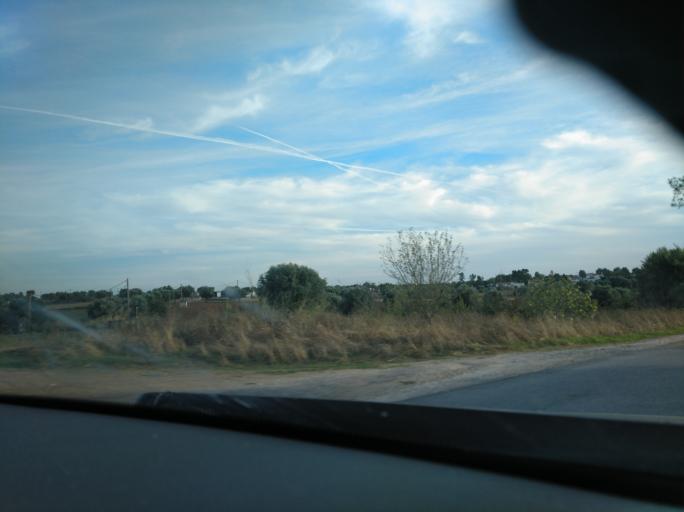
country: PT
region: Evora
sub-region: Arraiolos
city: Arraiolos
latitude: 38.8352
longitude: -7.8321
